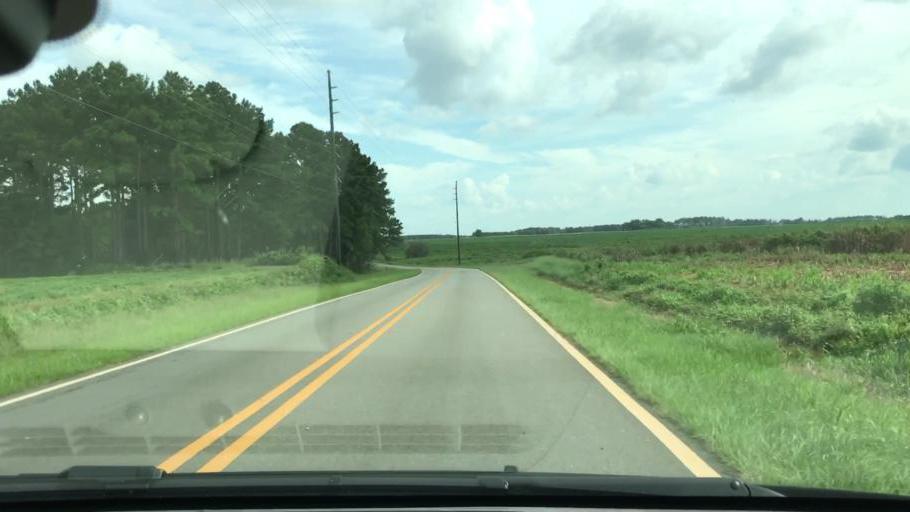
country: US
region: Georgia
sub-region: Clay County
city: Fort Gaines
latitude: 31.5342
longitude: -84.9586
